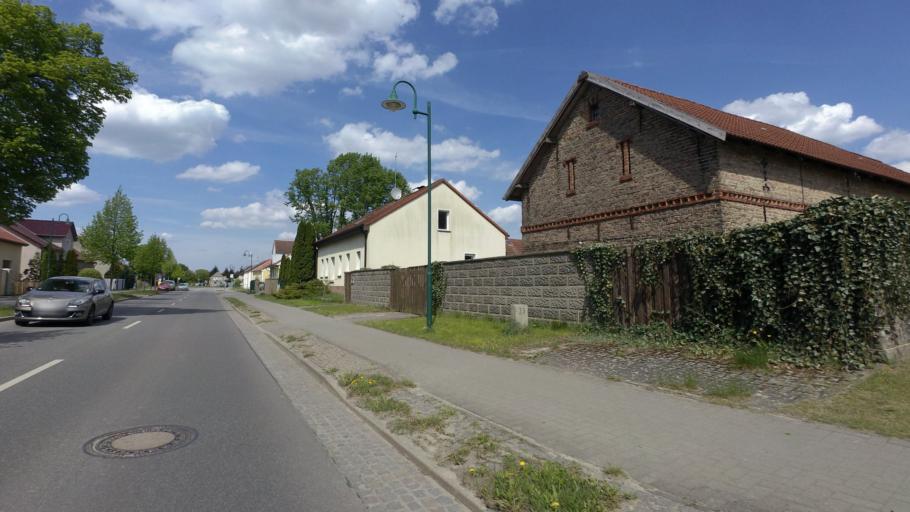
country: DE
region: Brandenburg
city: Wandlitz
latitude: 52.8003
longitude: 13.4789
